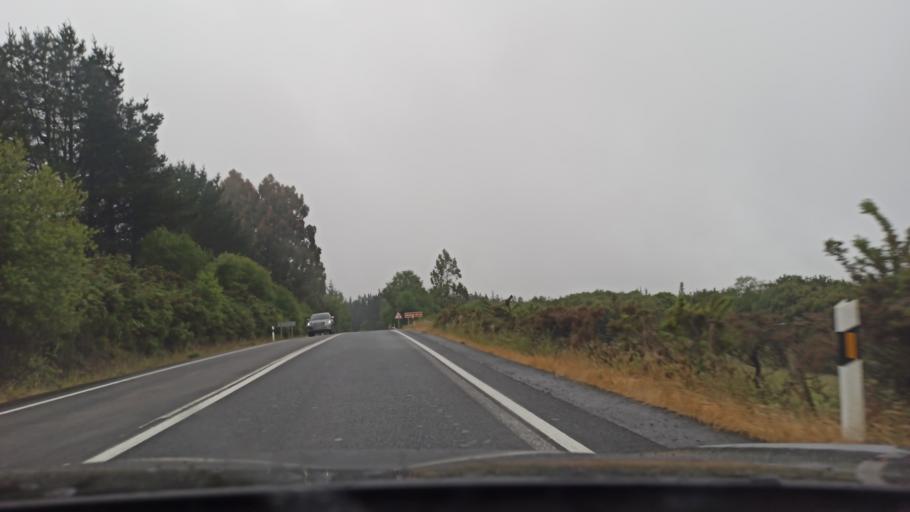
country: ES
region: Galicia
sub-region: Provincia de Lugo
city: Monterroso
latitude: 42.8296
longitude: -7.7620
